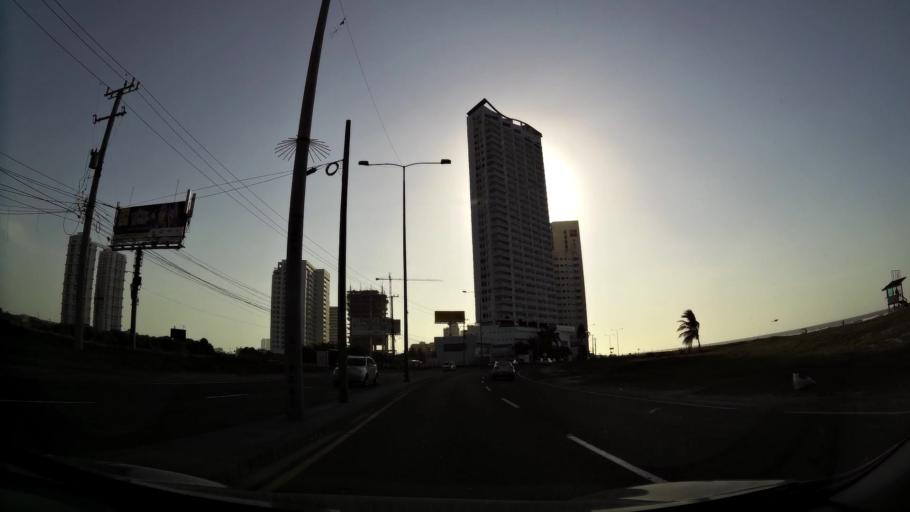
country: CO
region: Bolivar
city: Cartagena
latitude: 10.4374
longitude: -75.5334
